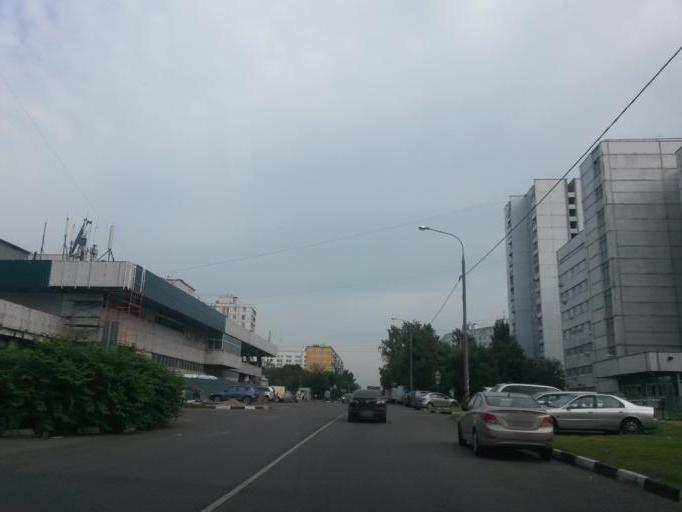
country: RU
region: Moscow
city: Orekhovo-Borisovo
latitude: 55.6080
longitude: 37.7329
